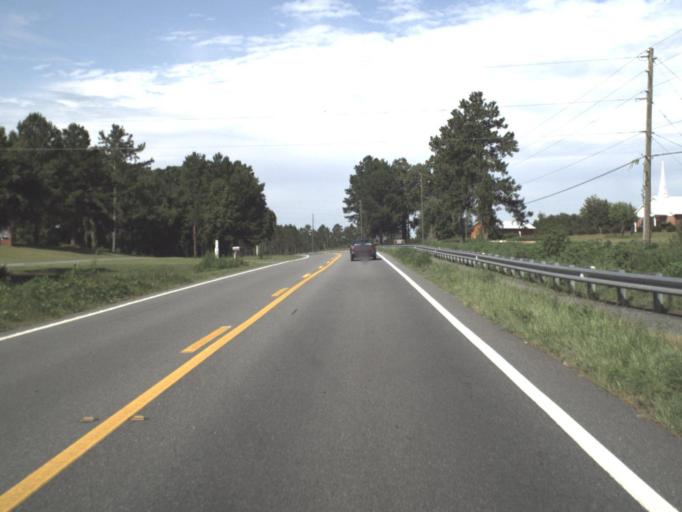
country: US
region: Florida
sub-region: Madison County
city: Madison
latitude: 30.4872
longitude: -83.3896
